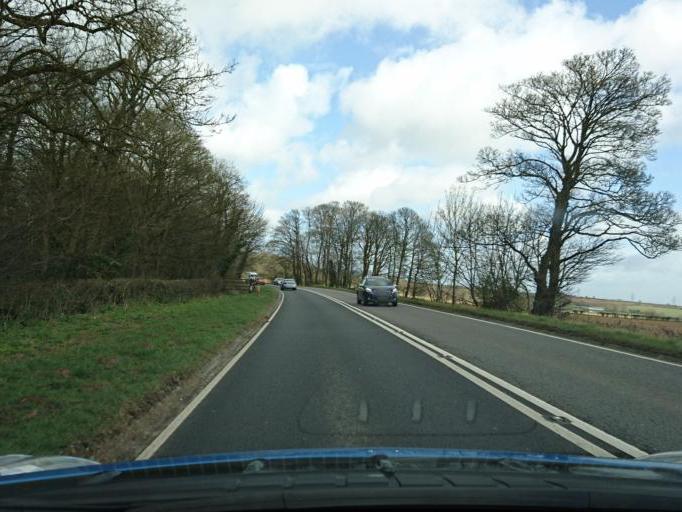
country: GB
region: England
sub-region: South Gloucestershire
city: Hinton
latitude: 51.4774
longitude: -2.3619
